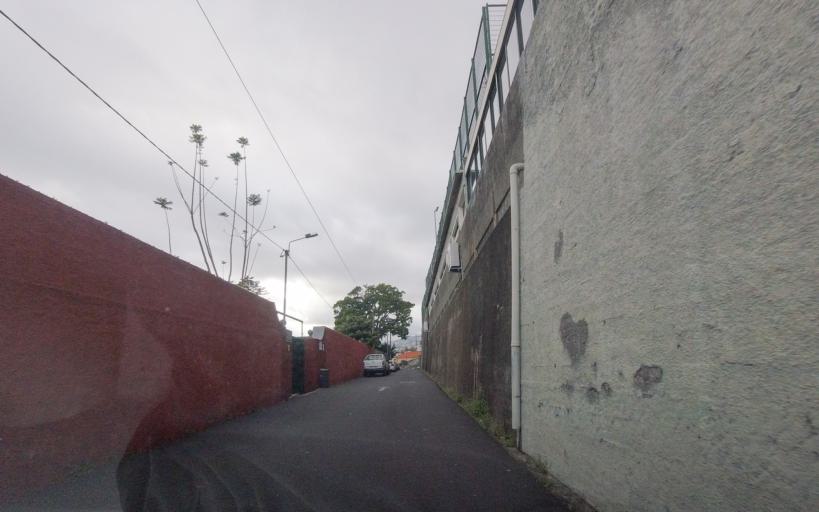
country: PT
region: Madeira
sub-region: Funchal
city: Nossa Senhora do Monte
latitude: 32.6564
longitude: -16.8974
